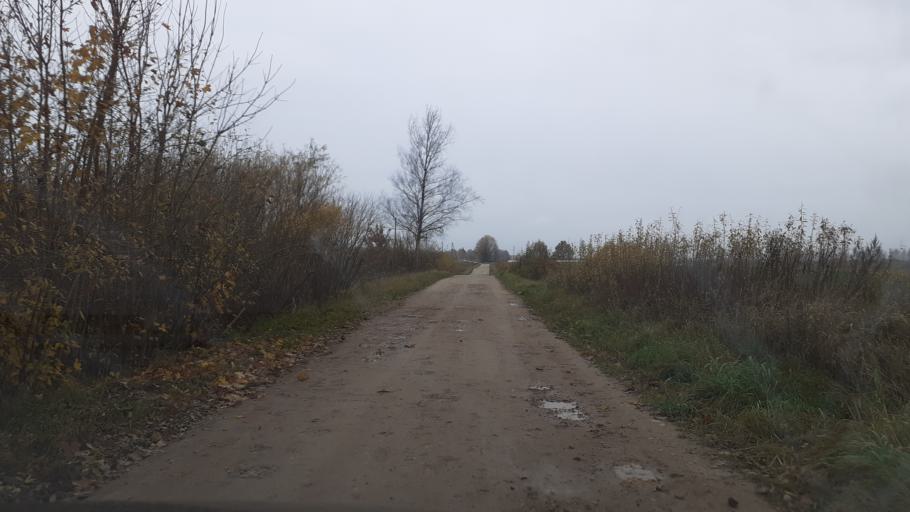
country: LV
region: Saldus Rajons
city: Saldus
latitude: 56.8628
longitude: 22.3519
